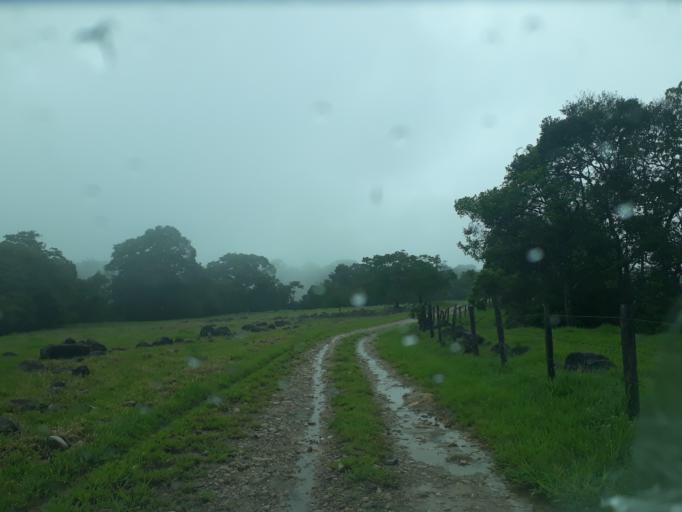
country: CO
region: Cundinamarca
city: Medina
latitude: 4.5309
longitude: -73.3707
